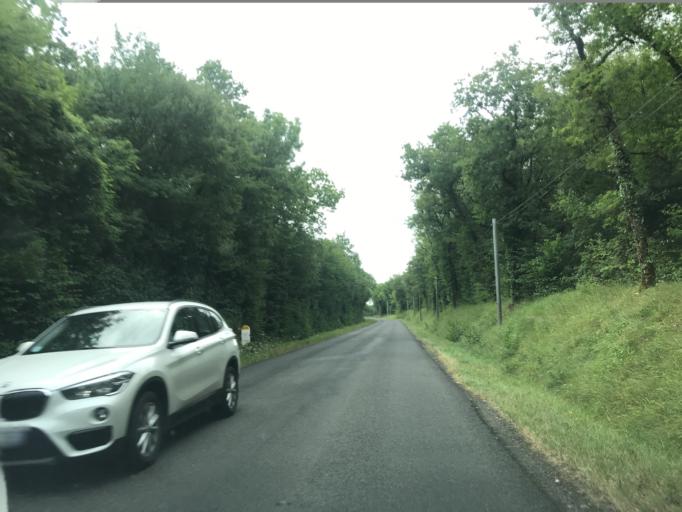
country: FR
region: Poitou-Charentes
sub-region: Departement de la Charente
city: Puymoyen
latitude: 45.5980
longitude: 0.1995
